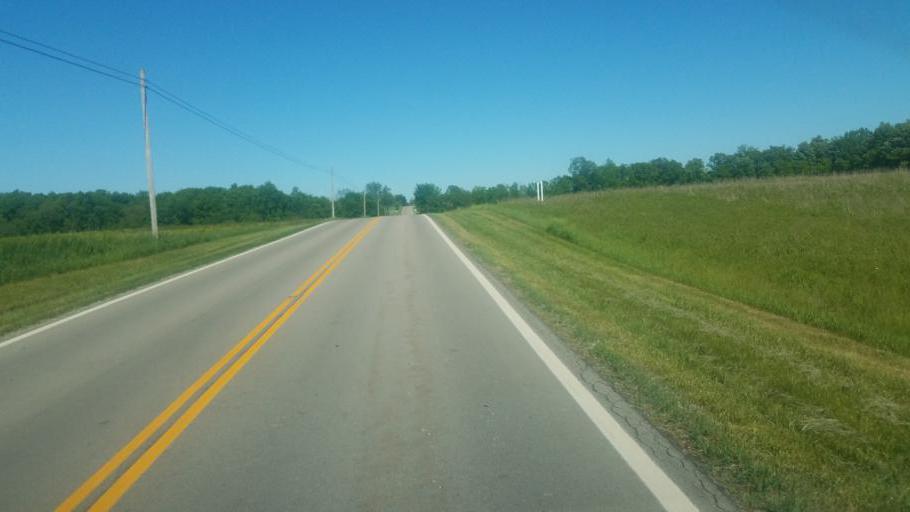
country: US
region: Ohio
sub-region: Logan County
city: Northwood
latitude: 40.4588
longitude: -83.6874
